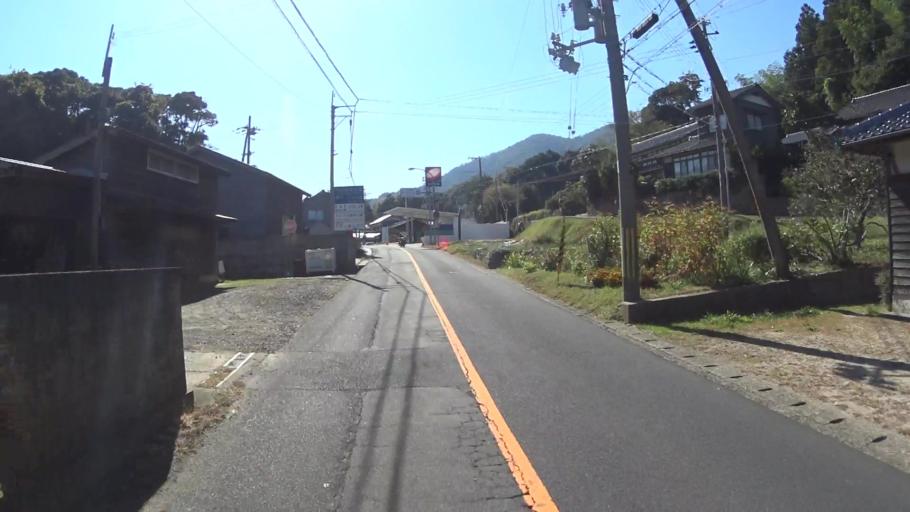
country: JP
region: Kyoto
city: Miyazu
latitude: 35.7506
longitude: 135.1673
